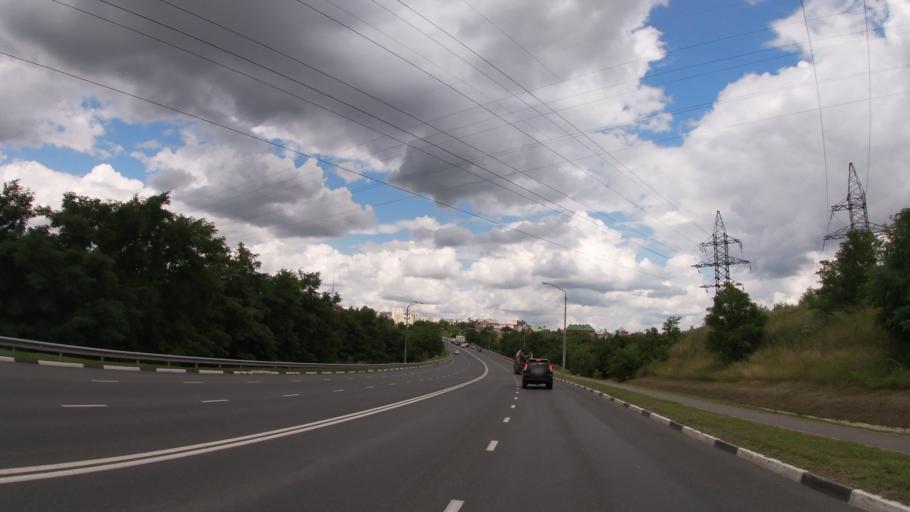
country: RU
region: Belgorod
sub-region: Belgorodskiy Rayon
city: Belgorod
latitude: 50.5580
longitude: 36.5861
